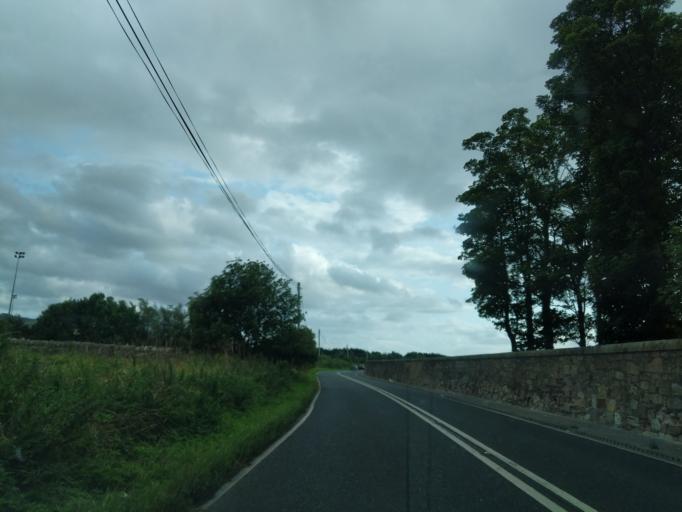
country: GB
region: Scotland
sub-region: Midlothian
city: Dalkeith
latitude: 55.9042
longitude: -3.0494
